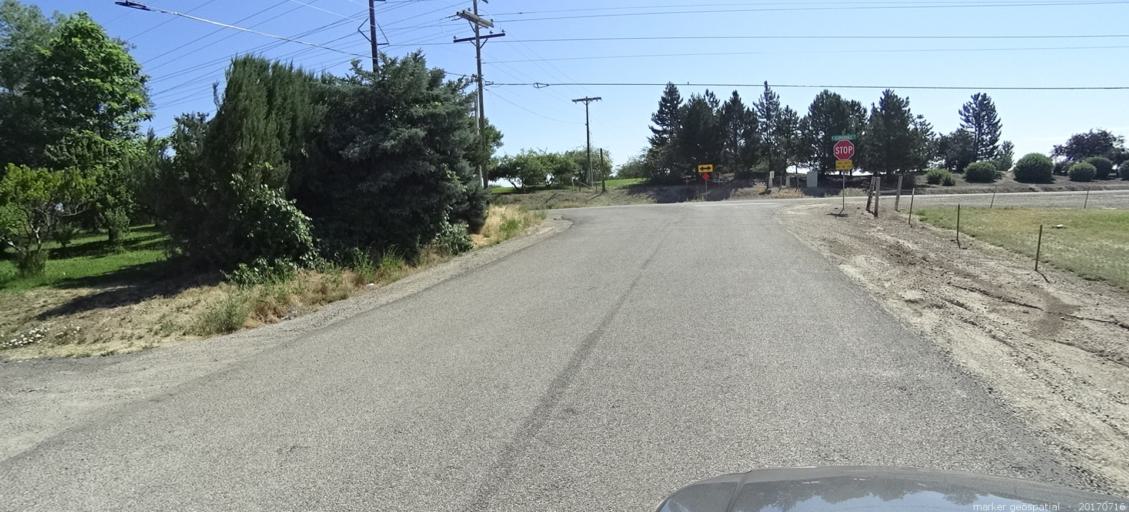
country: US
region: Idaho
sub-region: Ada County
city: Kuna
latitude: 43.5028
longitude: -116.3349
